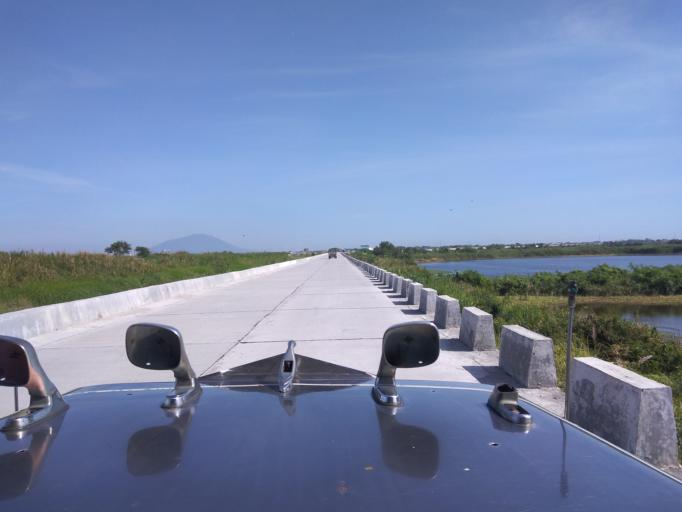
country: PH
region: Central Luzon
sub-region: Province of Pampanga
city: Minalin
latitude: 14.9764
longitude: 120.6811
